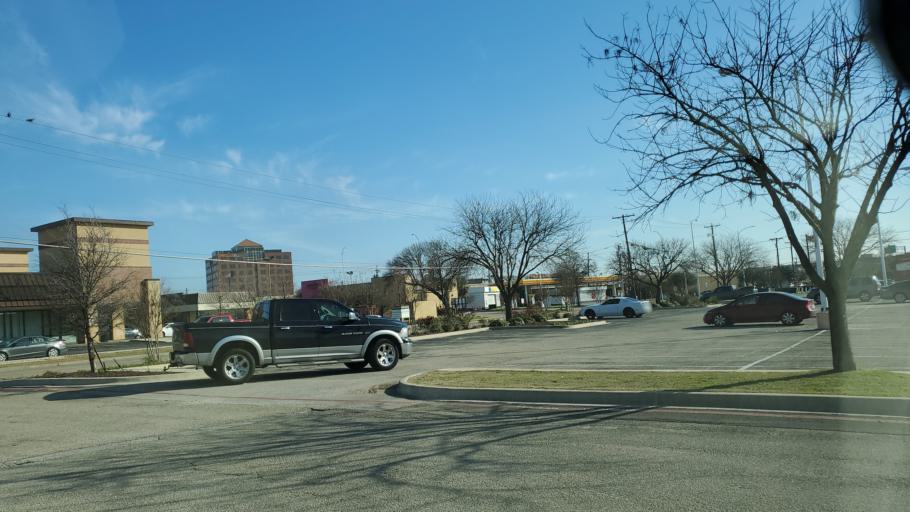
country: US
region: Texas
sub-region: Dallas County
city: Richardson
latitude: 32.9773
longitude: -96.7174
